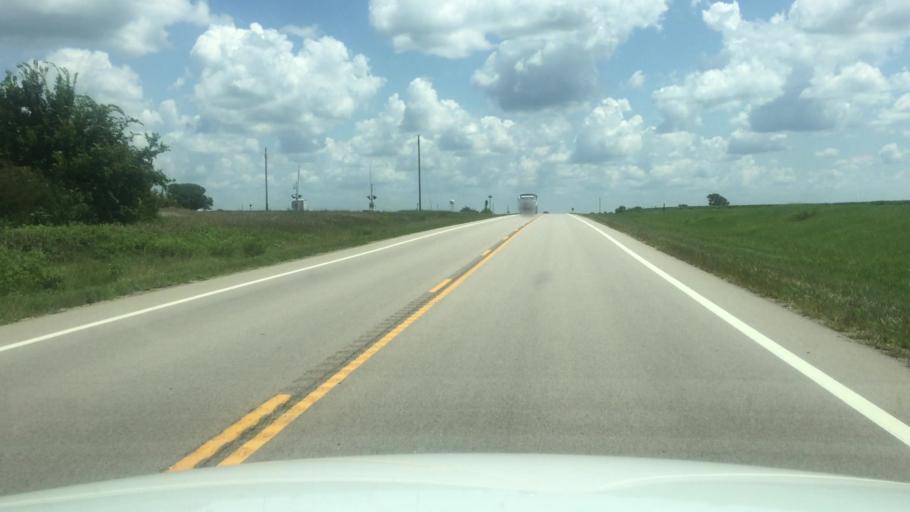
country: US
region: Kansas
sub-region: Brown County
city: Horton
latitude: 39.6529
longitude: -95.3639
